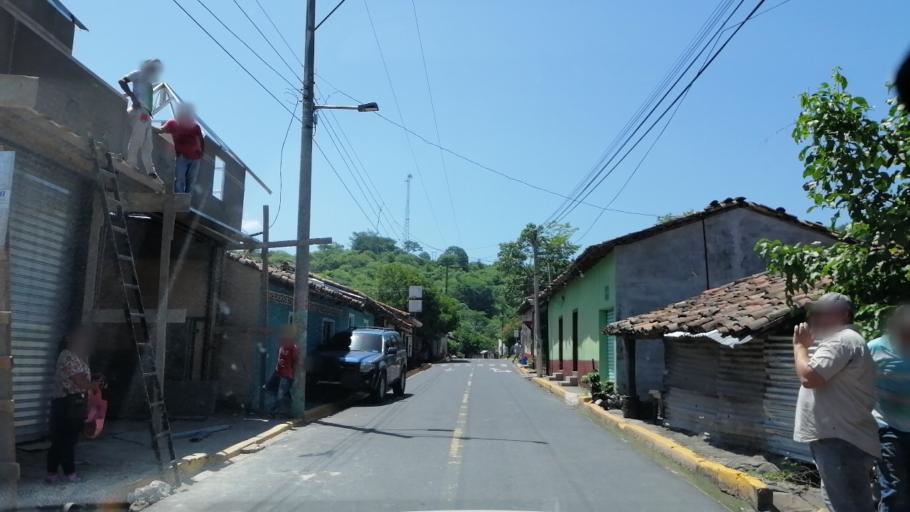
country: SV
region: San Miguel
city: Sesori
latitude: 13.8101
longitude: -88.4073
